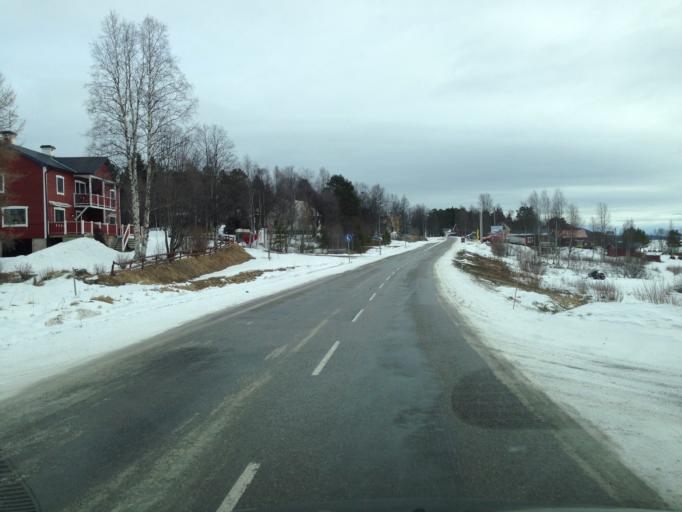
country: SE
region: Jaemtland
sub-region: Harjedalens Kommun
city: Sveg
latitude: 62.1122
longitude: 13.2746
